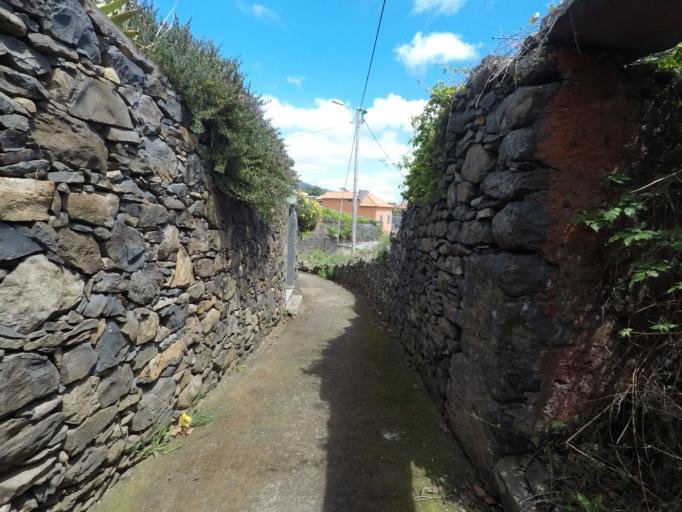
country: PT
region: Madeira
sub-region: Calheta
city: Estreito da Calheta
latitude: 32.7383
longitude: -17.1938
